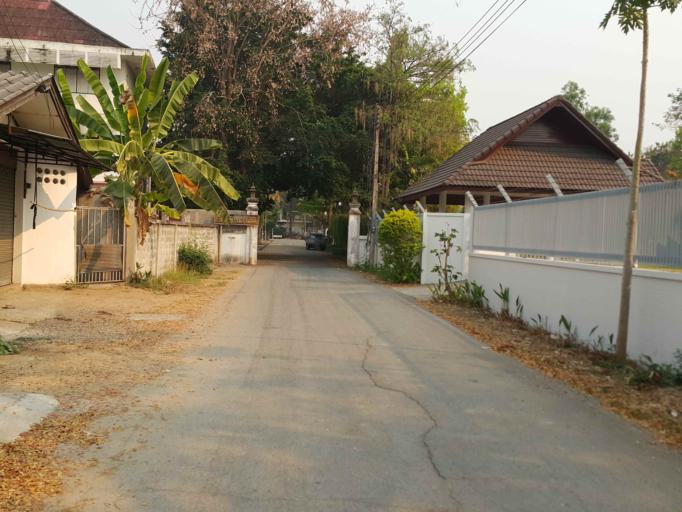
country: TH
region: Chiang Mai
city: San Kamphaeng
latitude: 18.7422
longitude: 99.1207
